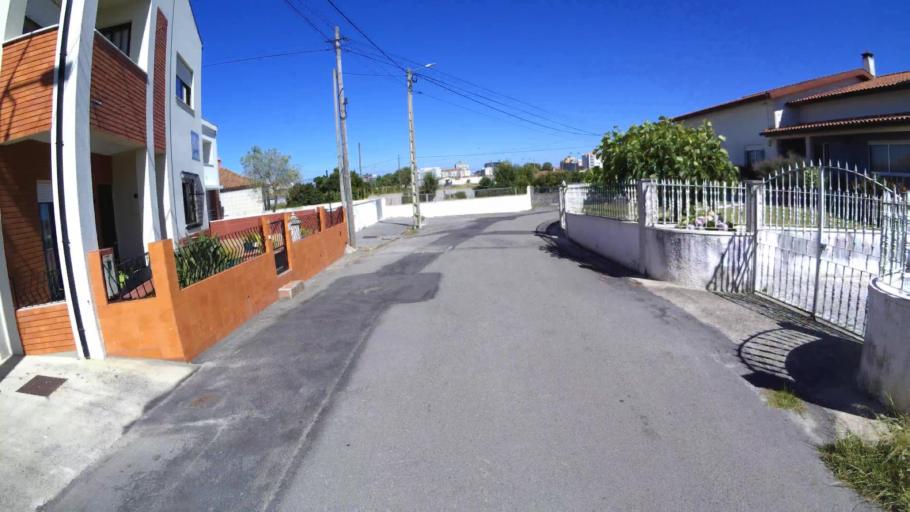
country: PT
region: Aveiro
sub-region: Aveiro
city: Aveiro
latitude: 40.6516
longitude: -8.6402
